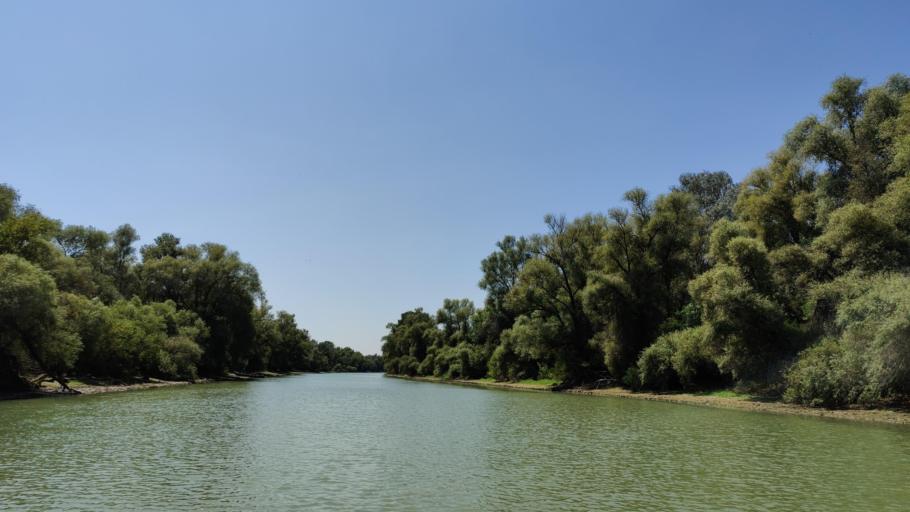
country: RO
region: Tulcea
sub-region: Comuna Nufaru
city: Nufaru
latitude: 45.2269
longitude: 28.8884
